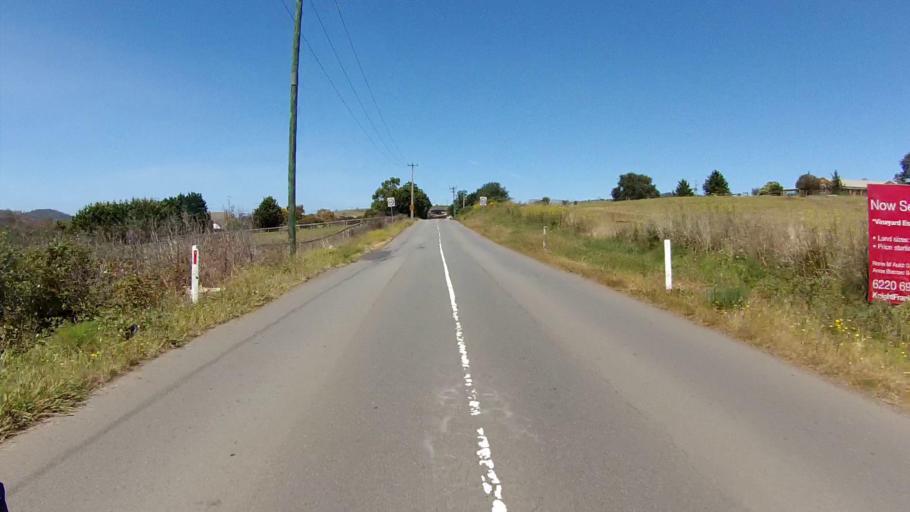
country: AU
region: Tasmania
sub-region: Clarence
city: Howrah
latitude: -42.8815
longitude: 147.4278
